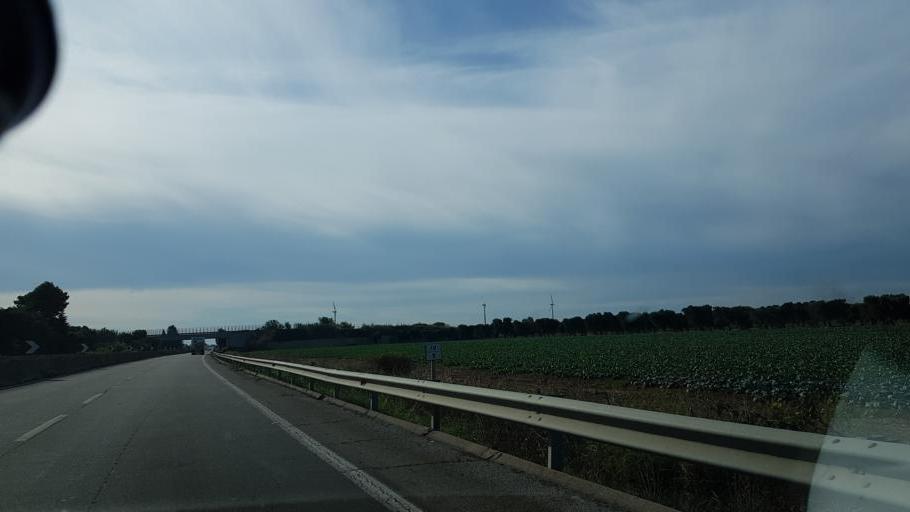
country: IT
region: Apulia
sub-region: Provincia di Brindisi
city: La Rosa
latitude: 40.5791
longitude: 17.9789
